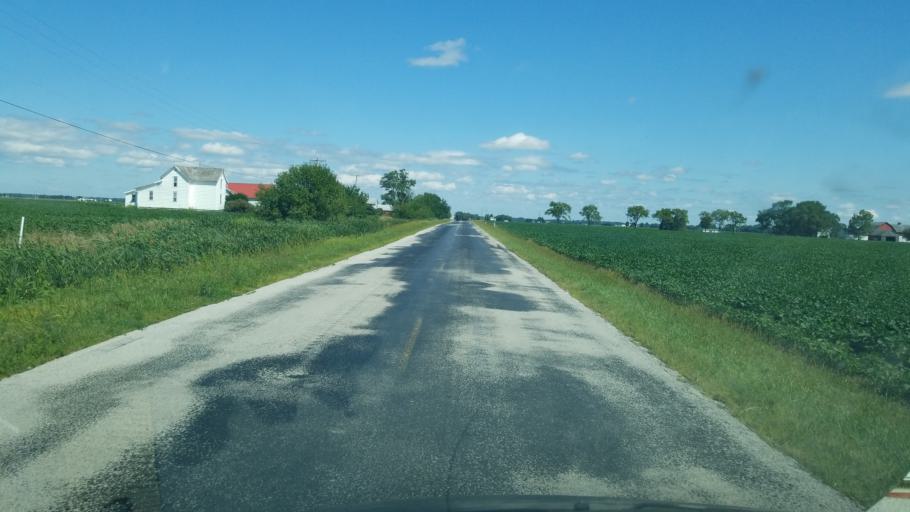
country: US
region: Ohio
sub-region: Wood County
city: Weston
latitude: 41.2929
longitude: -83.8440
